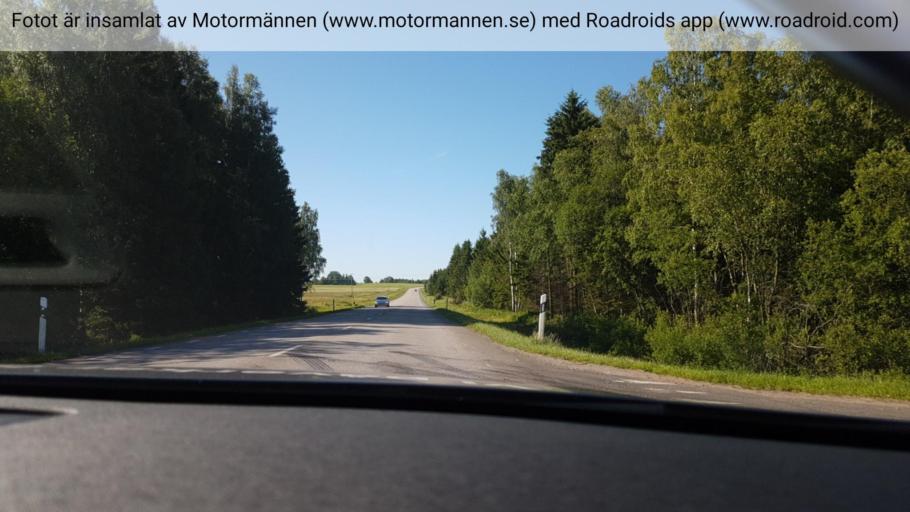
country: SE
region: Vaestra Goetaland
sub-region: Falkopings Kommun
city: Falkoeping
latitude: 58.1455
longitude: 13.5625
